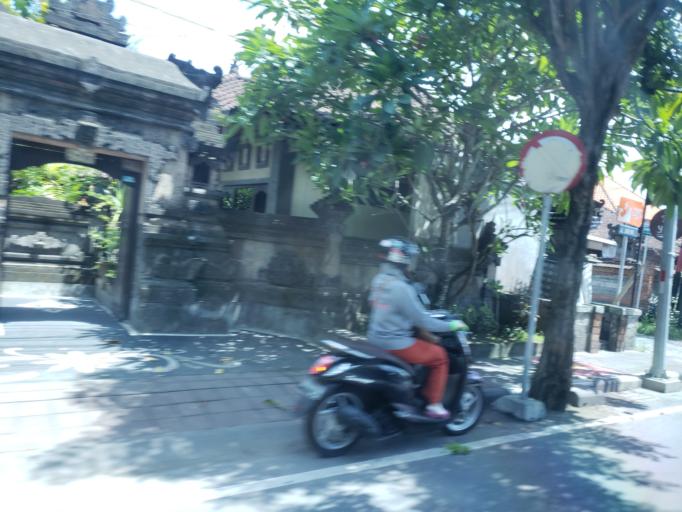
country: ID
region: Bali
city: Kelanabian
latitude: -8.7572
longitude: 115.1769
